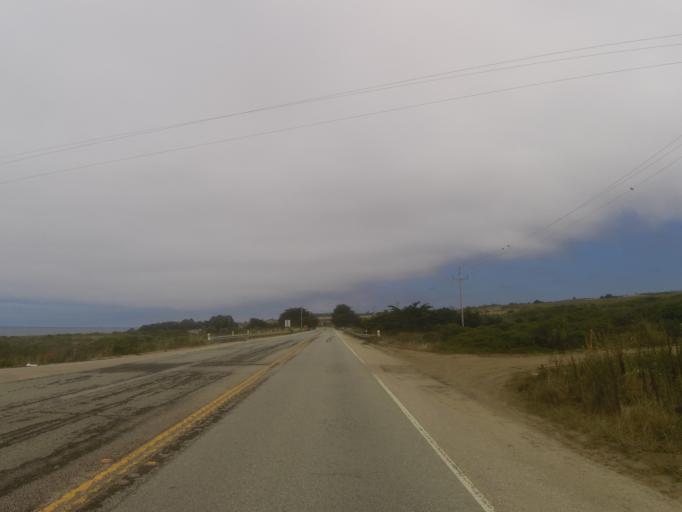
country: US
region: California
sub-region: San Mateo County
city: Portola Valley
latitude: 37.1989
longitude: -122.4006
